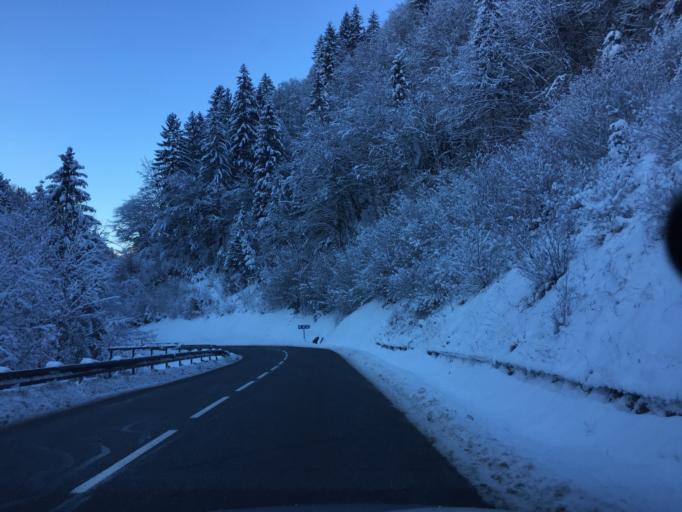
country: FR
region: Rhone-Alpes
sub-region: Departement de la Haute-Savoie
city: Saint-Paul-en-Chablais
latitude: 46.3344
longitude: 6.6165
